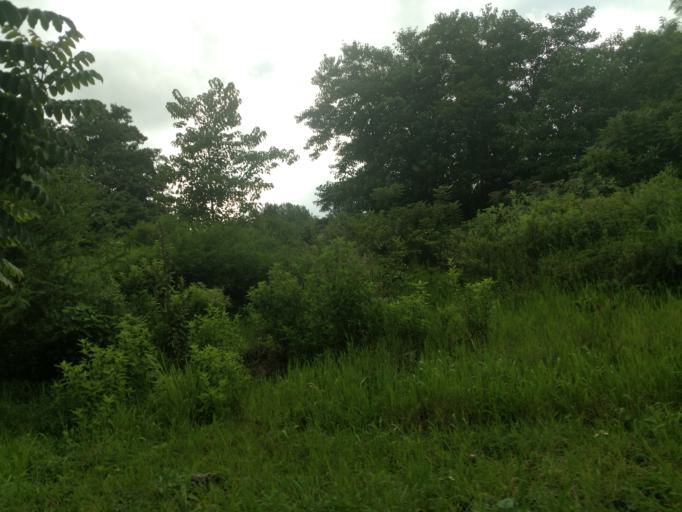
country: MX
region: Nayarit
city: Xalisco
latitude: 21.4756
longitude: -104.8599
